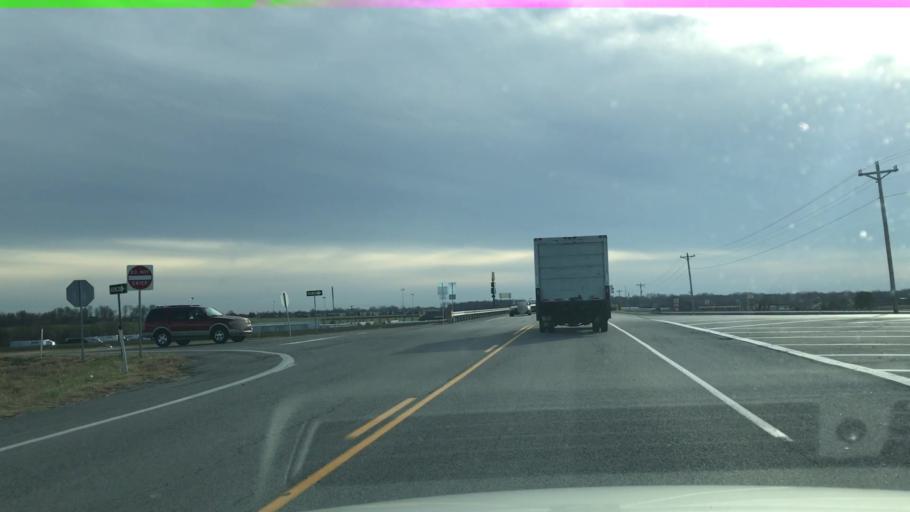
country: US
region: Kentucky
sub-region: Christian County
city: Oak Grove
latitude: 36.6837
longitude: -87.4038
